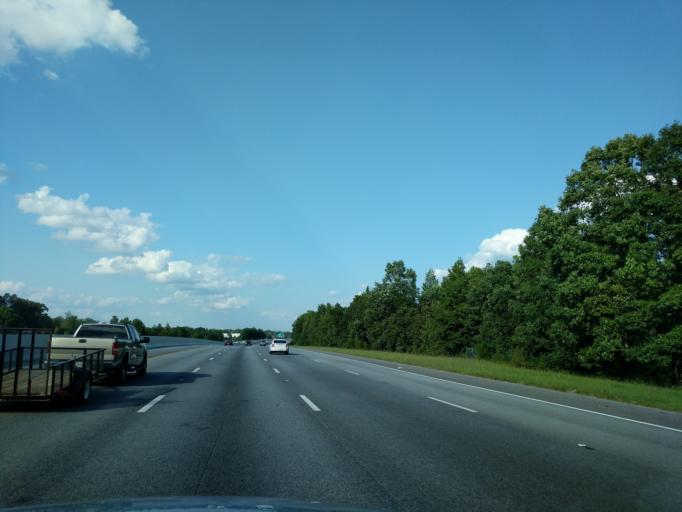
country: US
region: South Carolina
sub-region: Greenville County
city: Mauldin
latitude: 34.7591
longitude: -82.2837
